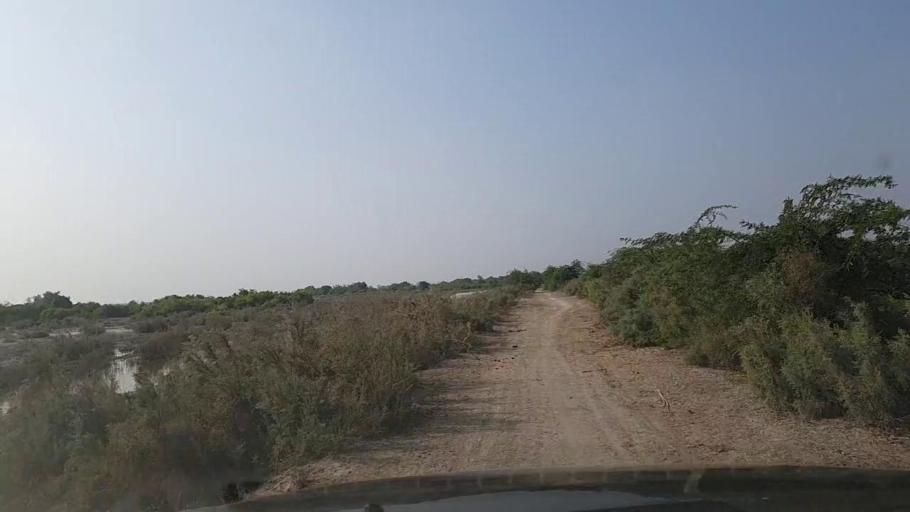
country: PK
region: Sindh
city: Mirpur Batoro
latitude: 24.6460
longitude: 68.2809
